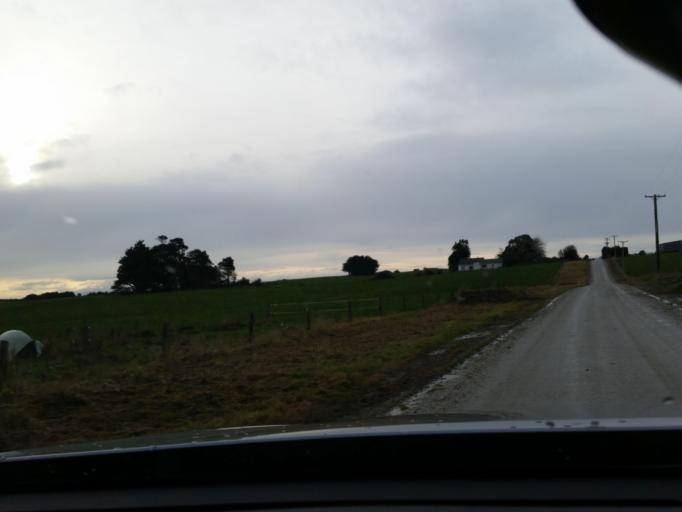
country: NZ
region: Southland
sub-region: Invercargill City
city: Invercargill
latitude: -46.4203
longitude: 168.5326
